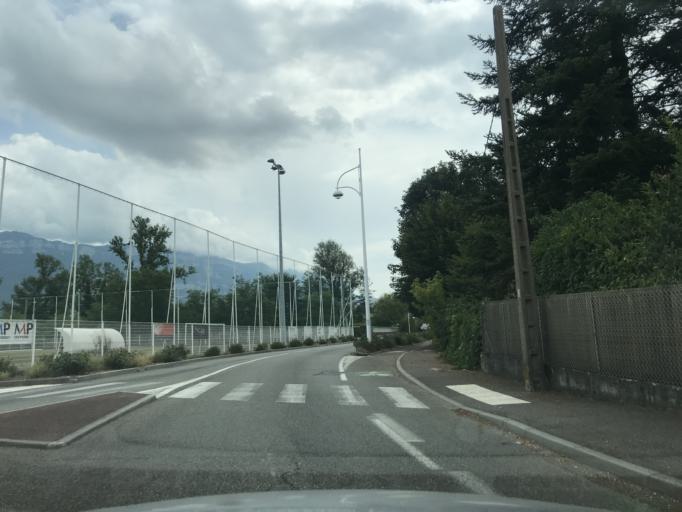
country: FR
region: Rhone-Alpes
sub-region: Departement de la Savoie
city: Brison-Saint-Innocent
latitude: 45.7021
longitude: 5.8914
